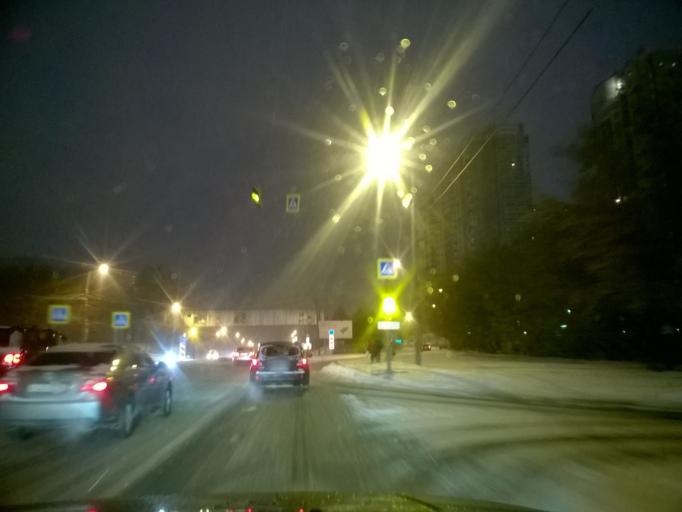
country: RU
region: Moscow
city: Amin'yevo
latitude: 55.6918
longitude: 37.4701
